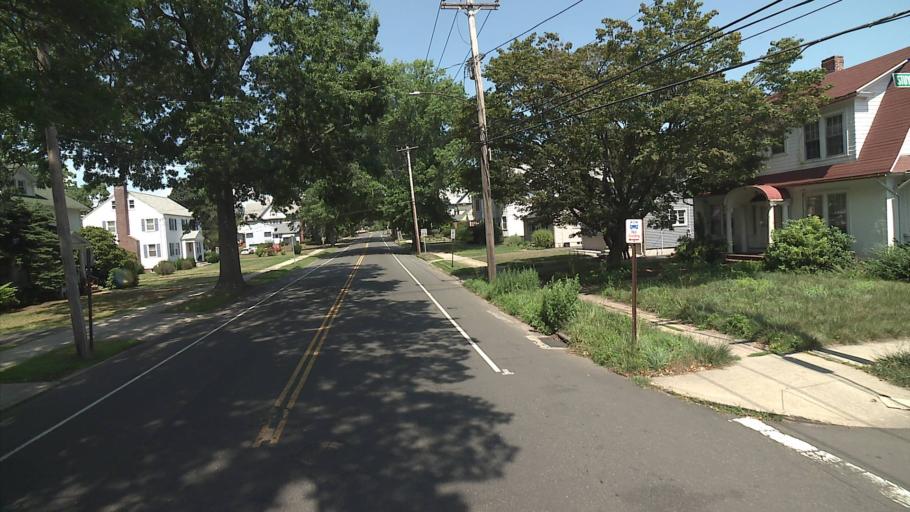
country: US
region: Connecticut
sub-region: New Haven County
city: East Haven
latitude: 41.2707
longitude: -72.8969
